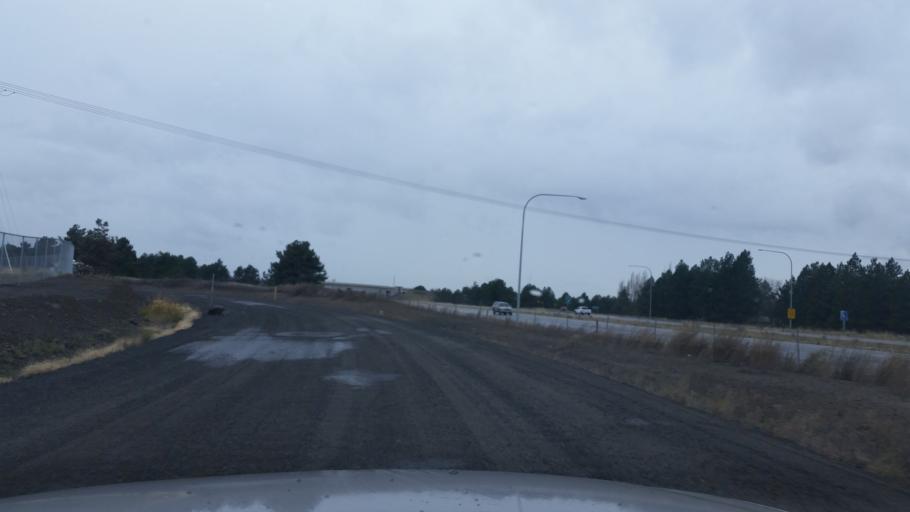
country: US
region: Washington
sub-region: Spokane County
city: Airway Heights
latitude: 47.5942
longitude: -117.5605
